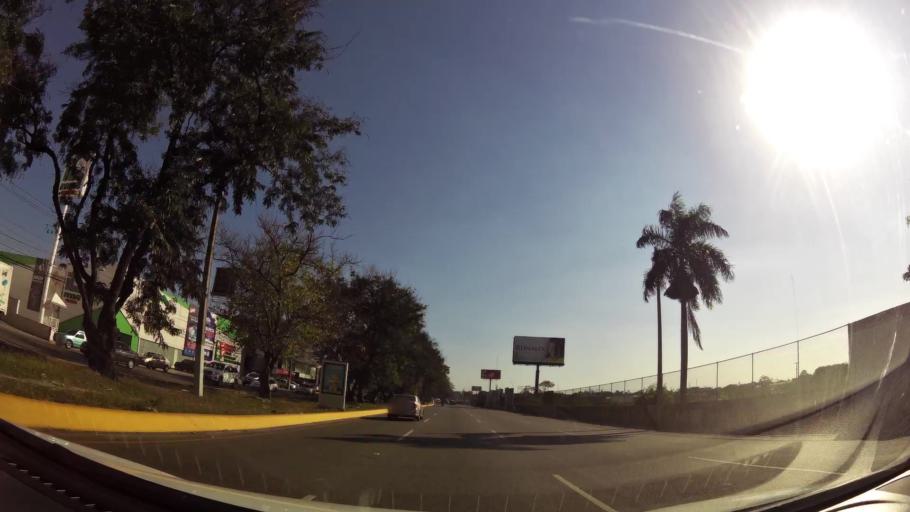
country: DO
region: Nacional
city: Bella Vista
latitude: 18.4613
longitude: -69.9694
